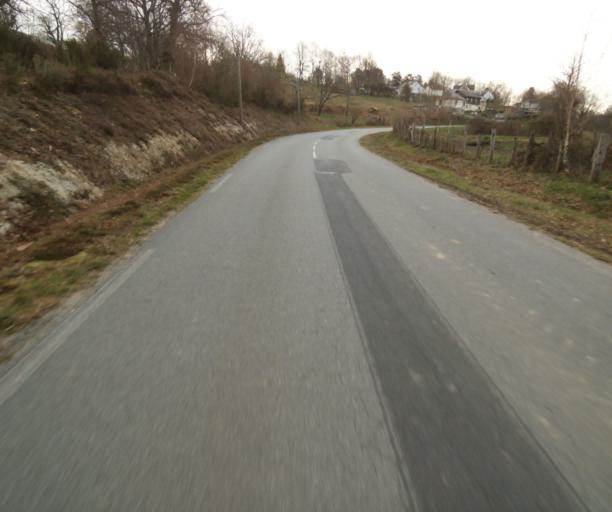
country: FR
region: Limousin
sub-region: Departement de la Correze
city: Correze
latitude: 45.4296
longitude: 1.8301
